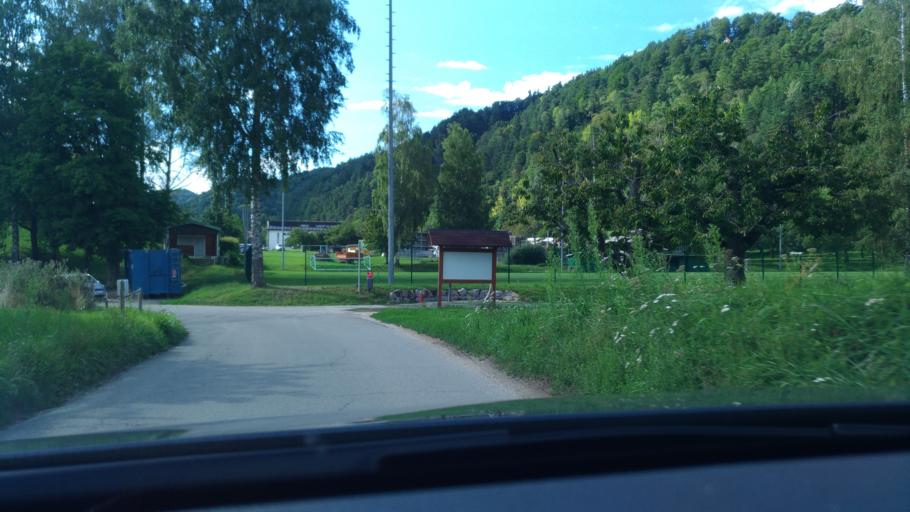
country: DE
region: Baden-Wuerttemberg
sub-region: Tuebingen Region
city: Sipplingen
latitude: 47.7956
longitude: 9.1086
